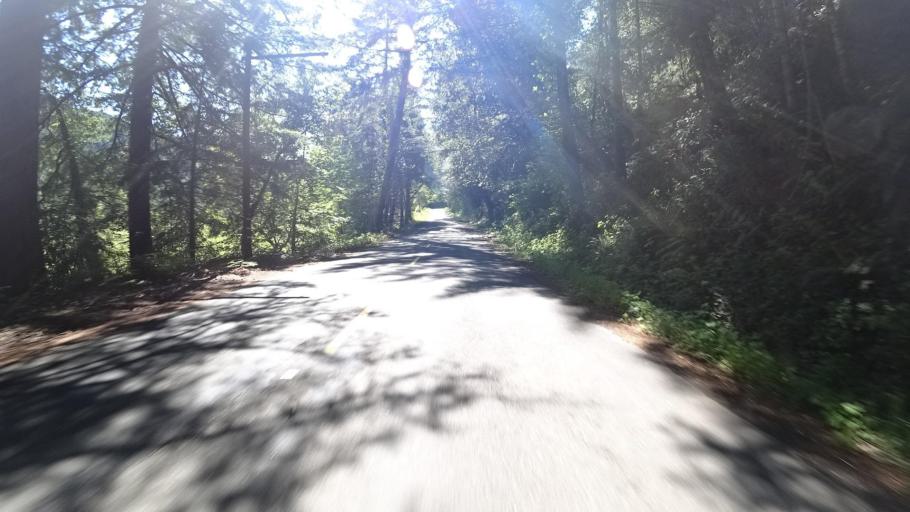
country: US
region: California
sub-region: Humboldt County
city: Rio Dell
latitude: 40.2686
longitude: -124.2028
